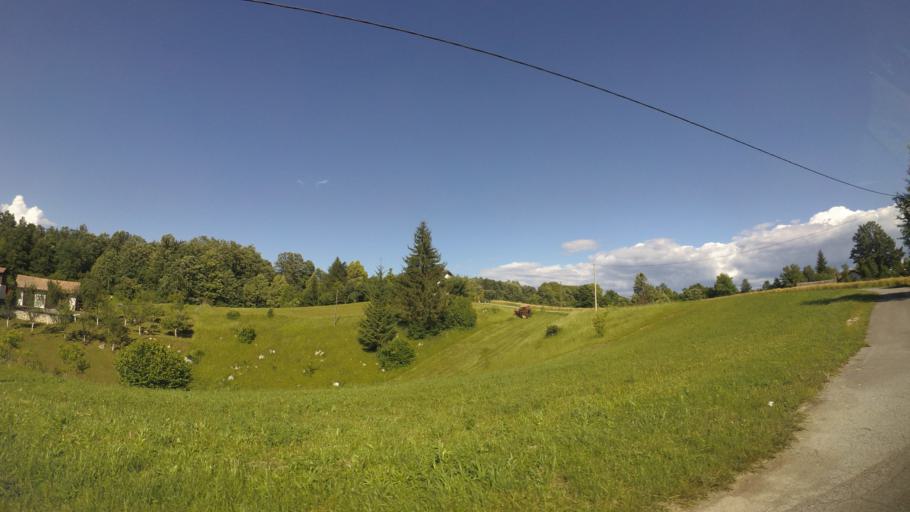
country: HR
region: Karlovacka
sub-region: Grad Karlovac
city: Slunj
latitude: 45.1512
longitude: 15.5656
